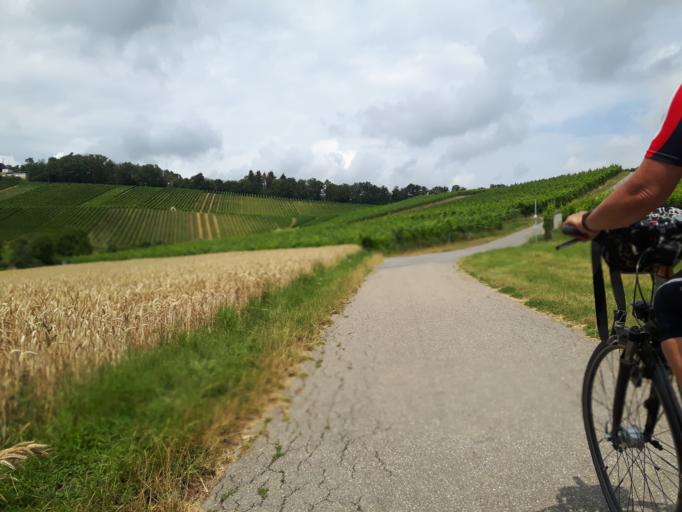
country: DE
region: Baden-Wuerttemberg
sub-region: Regierungsbezirk Stuttgart
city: Pfaffenhofen
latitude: 49.1041
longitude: 8.9669
